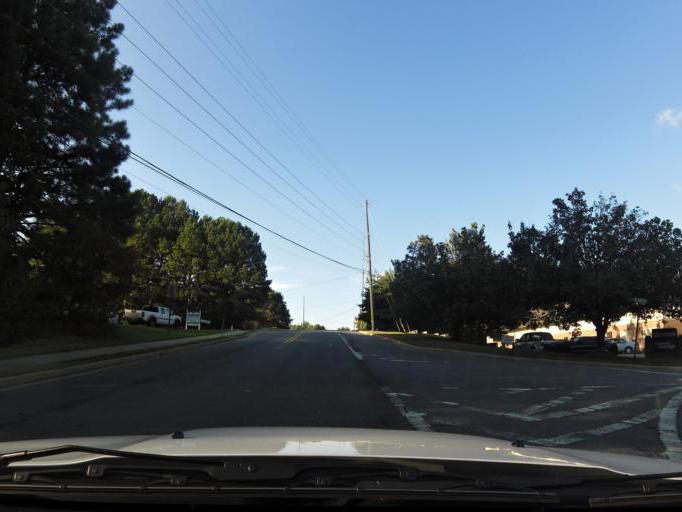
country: US
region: Georgia
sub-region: Cobb County
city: Kennesaw
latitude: 34.0461
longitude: -84.6160
